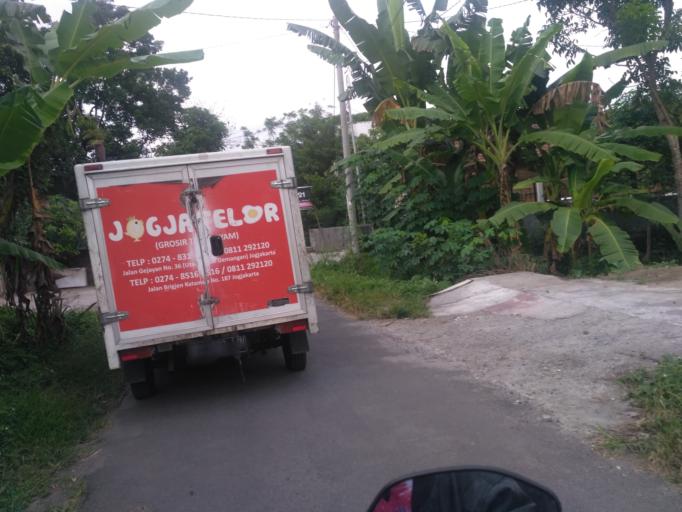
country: ID
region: Daerah Istimewa Yogyakarta
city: Melati
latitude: -7.7524
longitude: 110.3554
